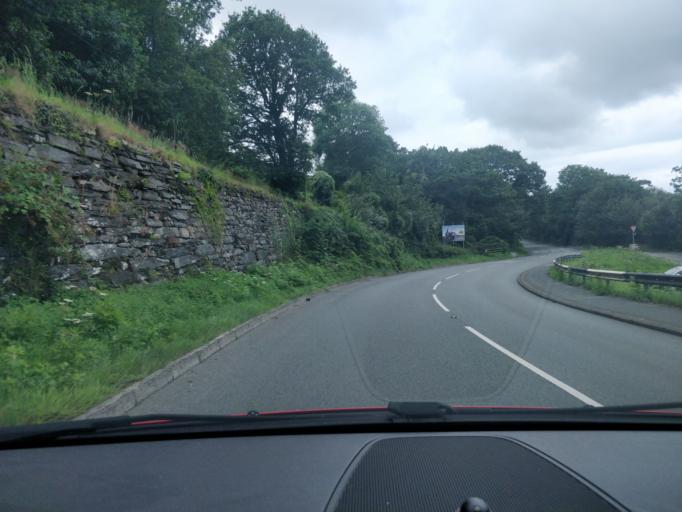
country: GB
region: Wales
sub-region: Gwynedd
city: Porthmadog
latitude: 52.9219
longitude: -4.1017
